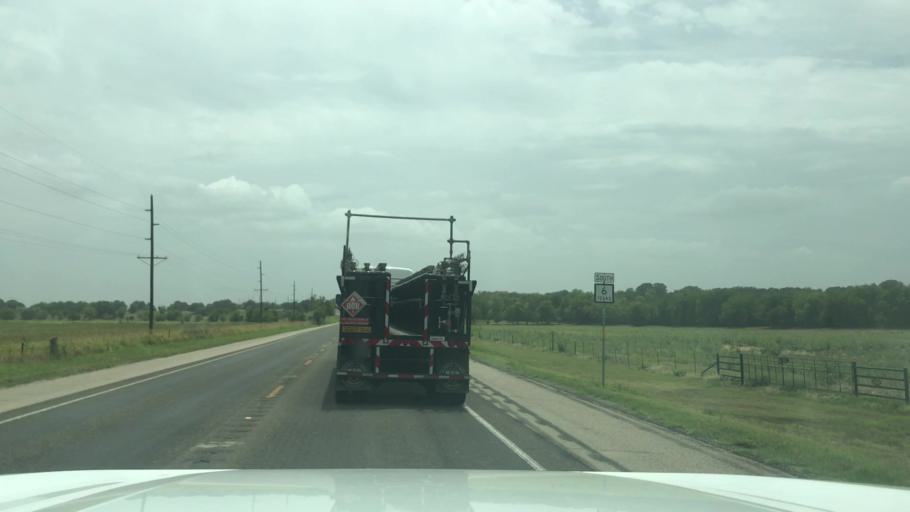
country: US
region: Texas
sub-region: Bosque County
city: Clifton
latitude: 31.7133
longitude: -97.5466
